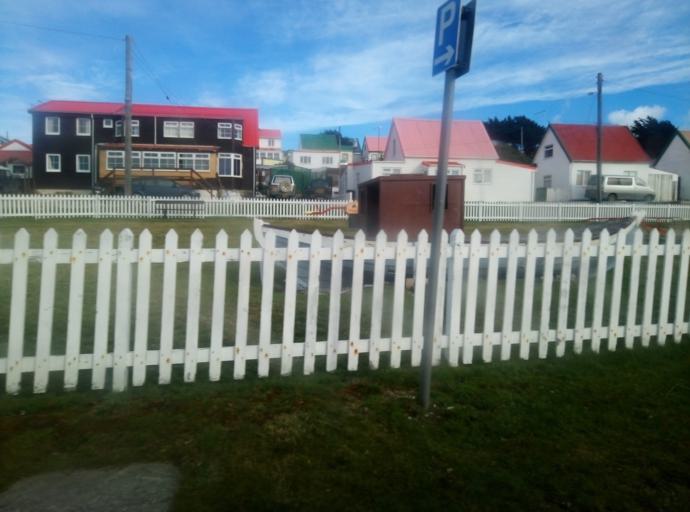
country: FK
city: Stanley
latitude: -51.6926
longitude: -57.8654
